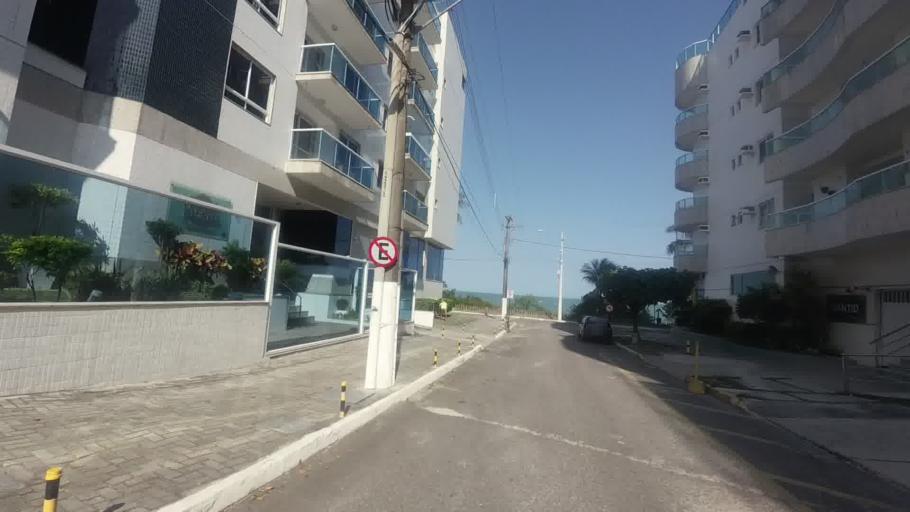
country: BR
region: Espirito Santo
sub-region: Guarapari
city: Guarapari
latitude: -20.7293
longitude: -40.5285
